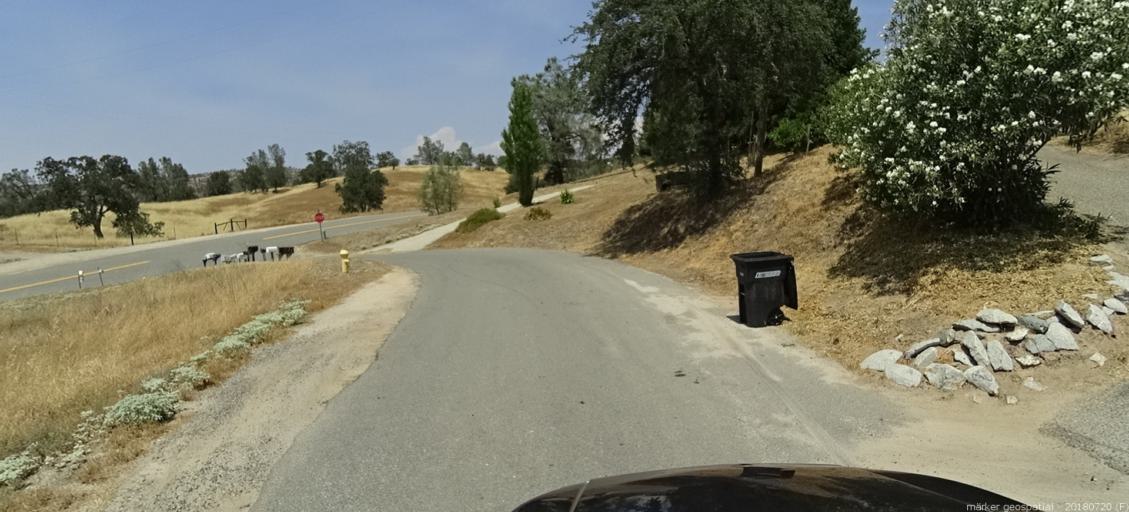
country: US
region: California
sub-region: Madera County
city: Yosemite Lakes
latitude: 37.1623
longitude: -119.8454
